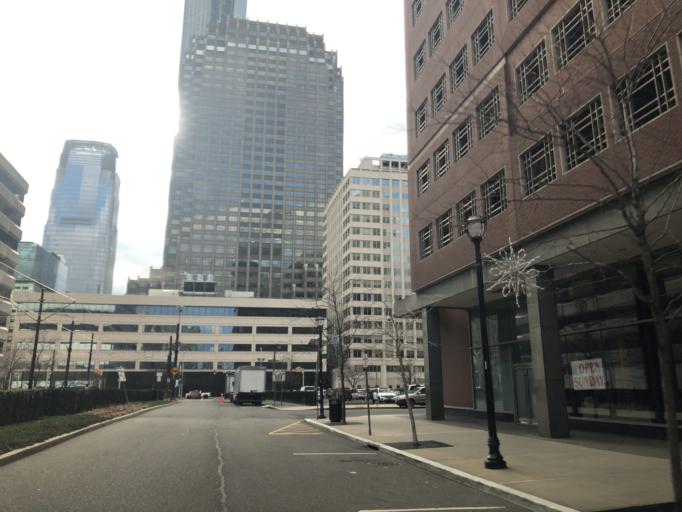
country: US
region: New Jersey
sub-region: Hudson County
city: Hoboken
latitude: 40.7184
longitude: -74.0345
